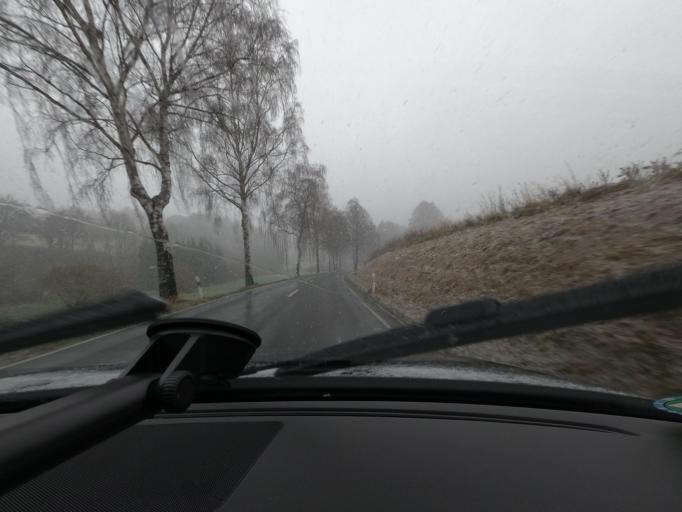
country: DE
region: North Rhine-Westphalia
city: Marsberg
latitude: 51.5068
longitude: 8.8910
